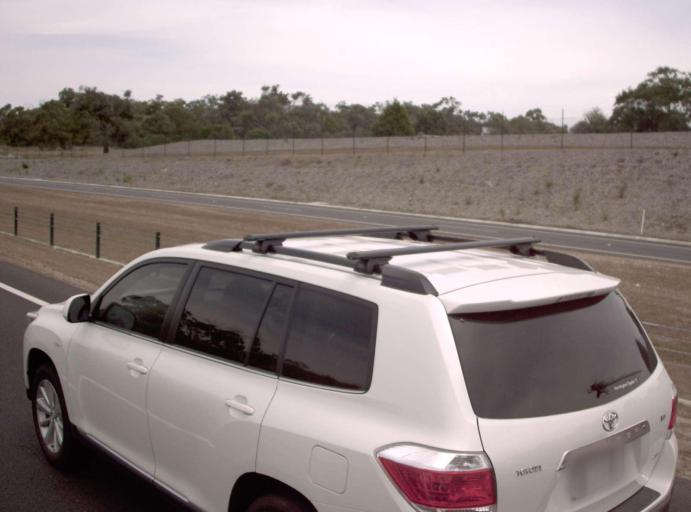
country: AU
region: Victoria
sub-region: Frankston
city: Langwarrin
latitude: -38.1702
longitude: 145.1638
